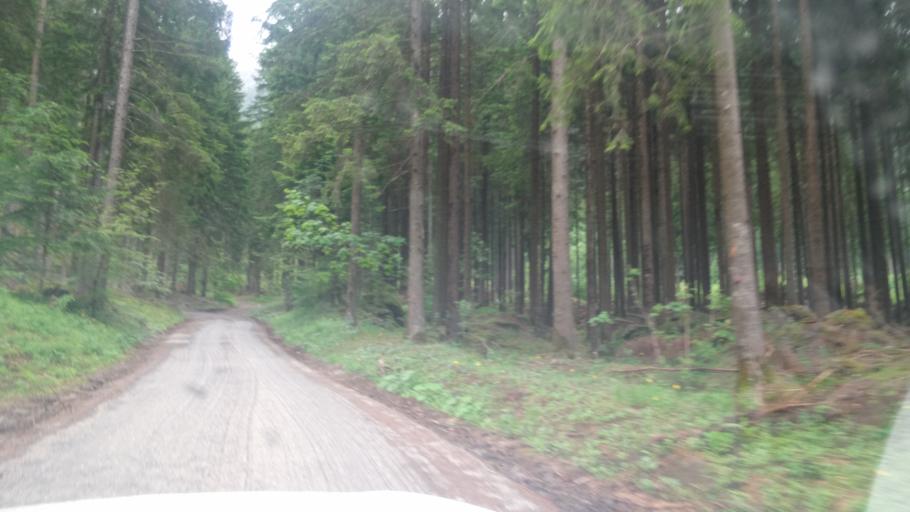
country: IT
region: Friuli Venezia Giulia
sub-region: Provincia di Udine
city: Paluzza
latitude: 46.5676
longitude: 13.0151
